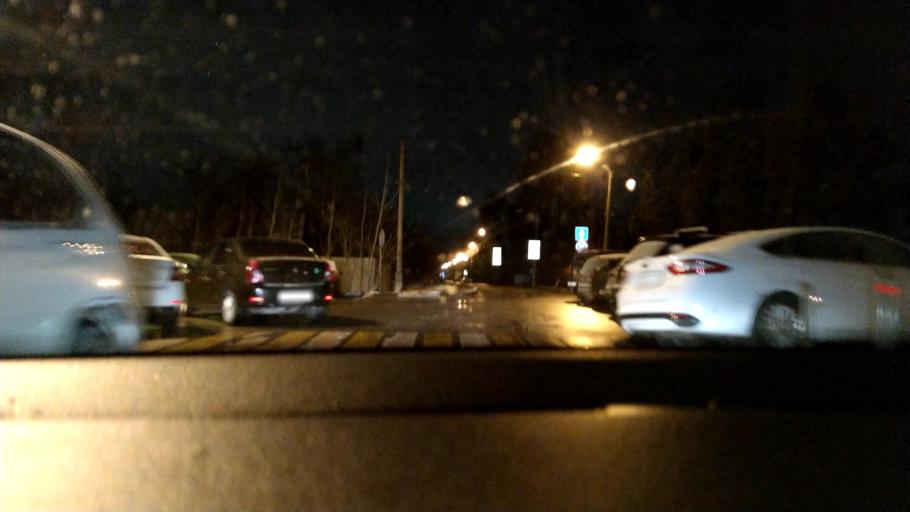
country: RU
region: Moscow
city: Strogino
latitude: 55.8616
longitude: 37.3930
